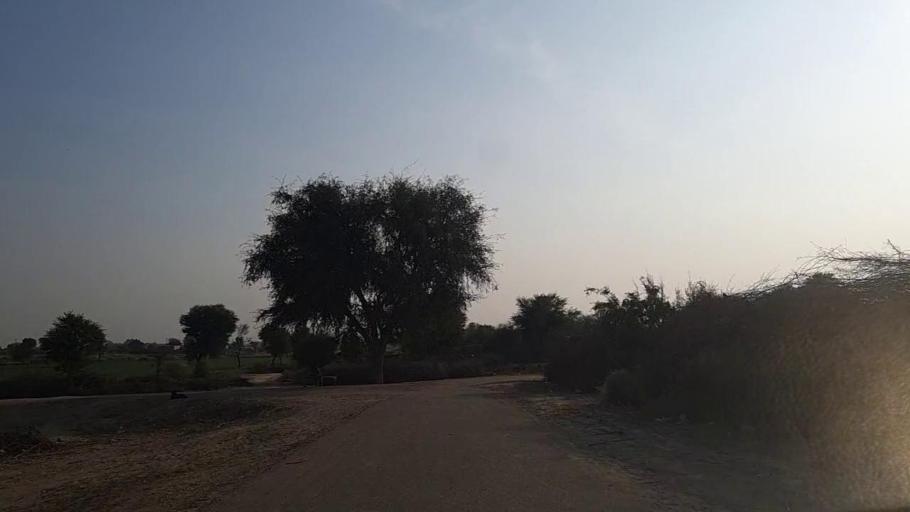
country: PK
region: Sindh
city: Jam Sahib
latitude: 26.4458
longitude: 68.5831
